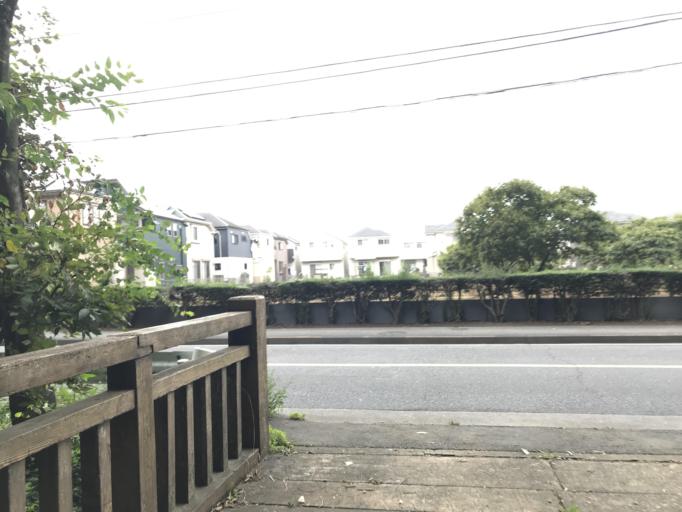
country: JP
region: Tokyo
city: Higashimurayama-shi
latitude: 35.7595
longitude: 139.4980
